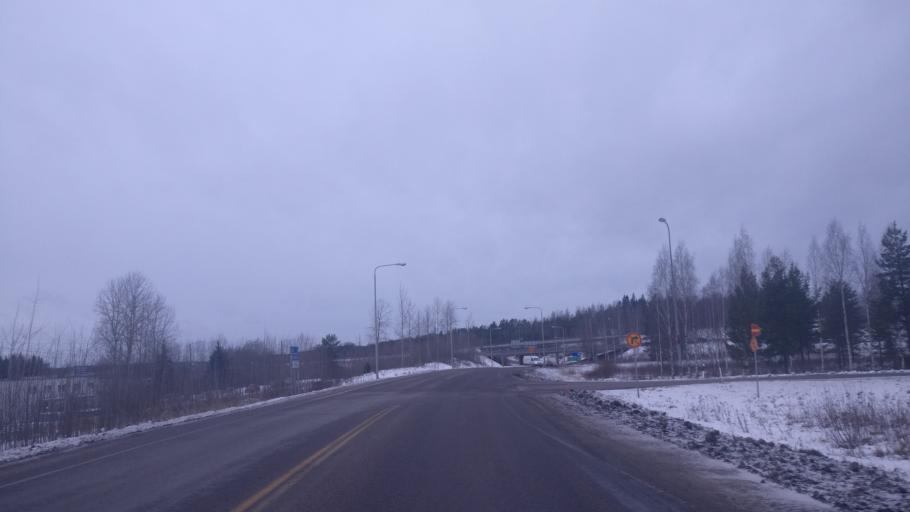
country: FI
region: Paijanne Tavastia
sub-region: Lahti
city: Lahti
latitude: 60.9670
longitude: 25.7204
